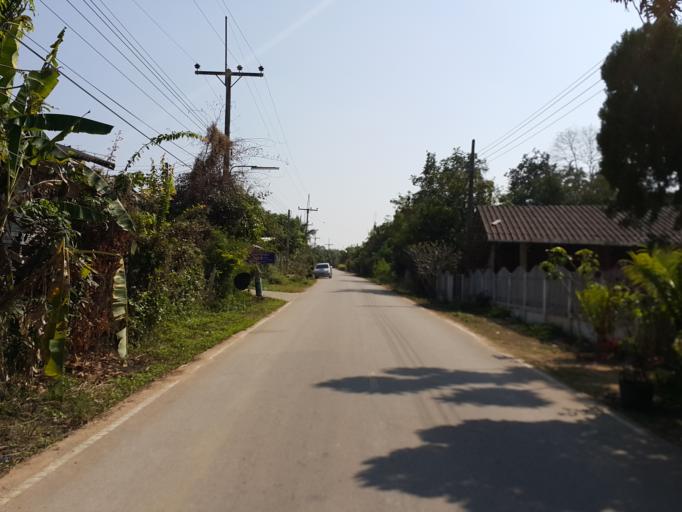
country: TH
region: Lampang
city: Wang Nuea
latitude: 19.0472
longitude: 99.6231
